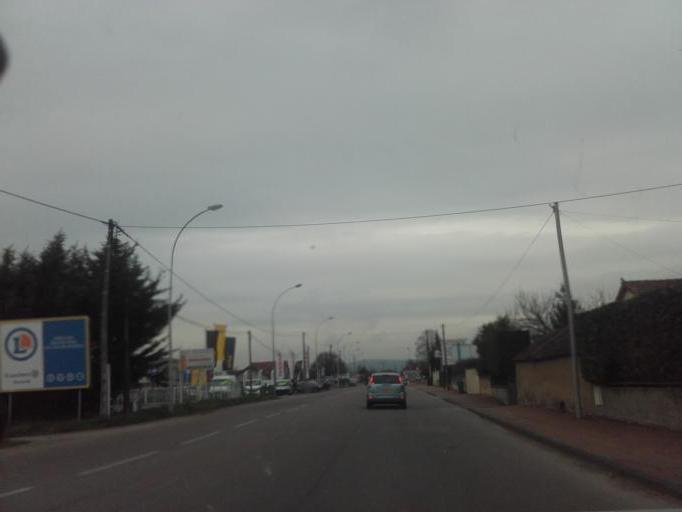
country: FR
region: Bourgogne
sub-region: Departement de la Cote-d'Or
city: Beaune
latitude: 47.0187
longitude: 4.8606
